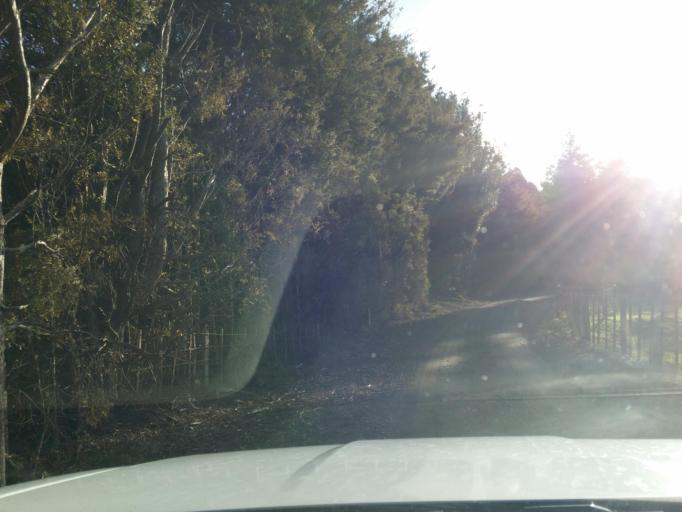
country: NZ
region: Northland
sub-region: Kaipara District
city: Dargaville
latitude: -35.7543
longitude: 173.6624
